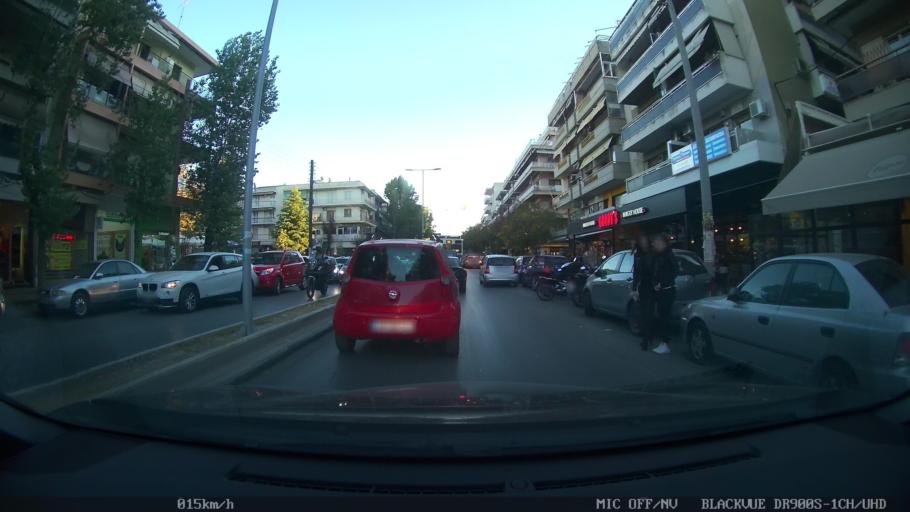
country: GR
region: Central Macedonia
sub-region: Nomos Thessalonikis
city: Triandria
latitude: 40.6032
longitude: 22.9691
